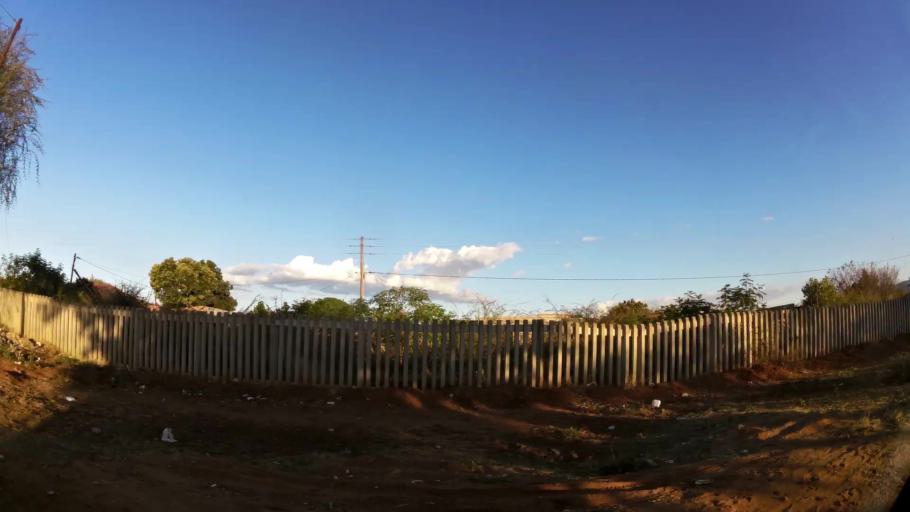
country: ZA
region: Limpopo
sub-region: Waterberg District Municipality
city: Mokopane
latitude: -24.1426
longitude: 28.9933
